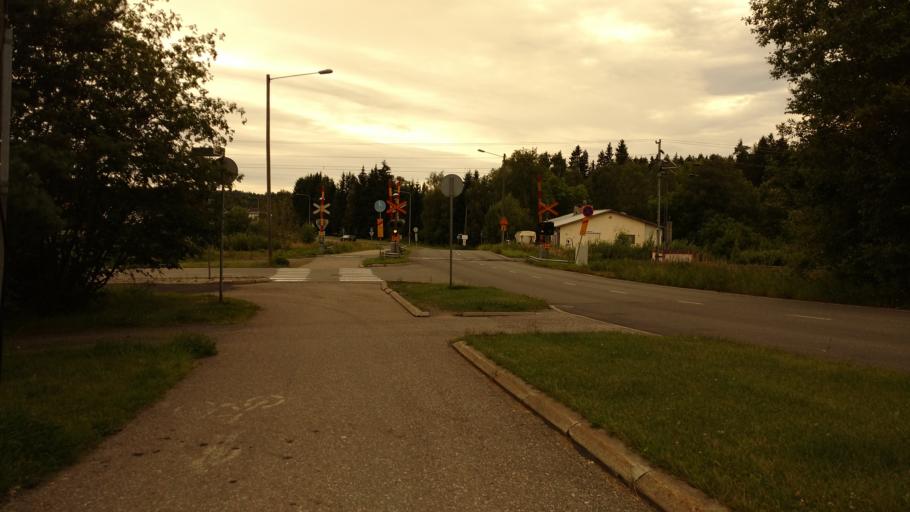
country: FI
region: Varsinais-Suomi
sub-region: Turku
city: Kaarina
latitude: 60.4392
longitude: 22.3559
